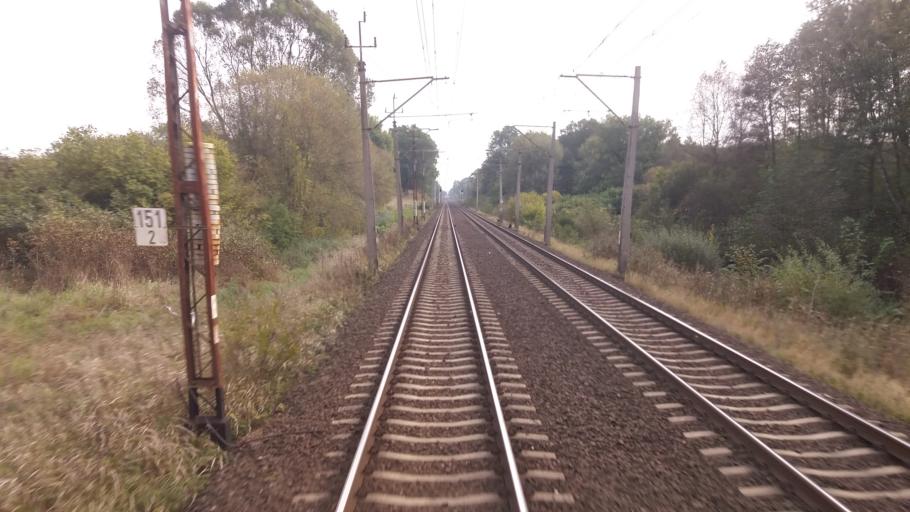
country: PL
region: West Pomeranian Voivodeship
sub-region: Powiat stargardzki
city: Dolice
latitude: 53.1924
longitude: 15.2342
